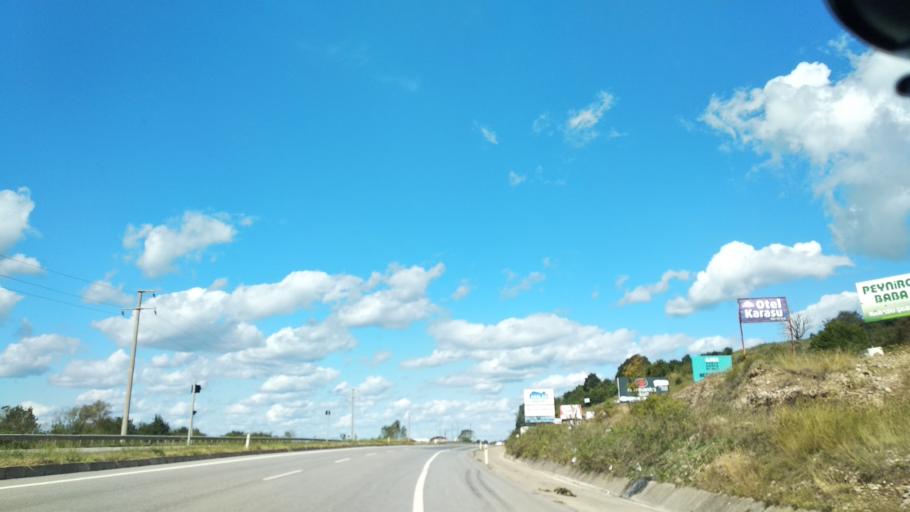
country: TR
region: Sakarya
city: Karasu
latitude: 41.0958
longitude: 30.6537
